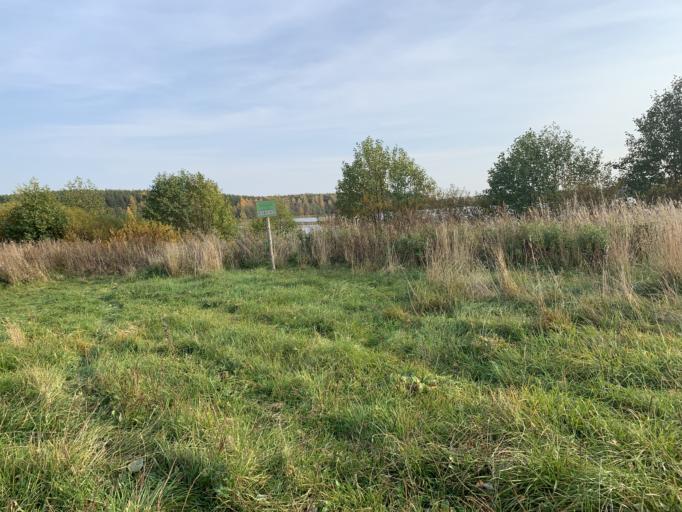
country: RU
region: Jaroslavl
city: Porech'ye-Rybnoye
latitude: 56.9785
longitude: 39.3860
